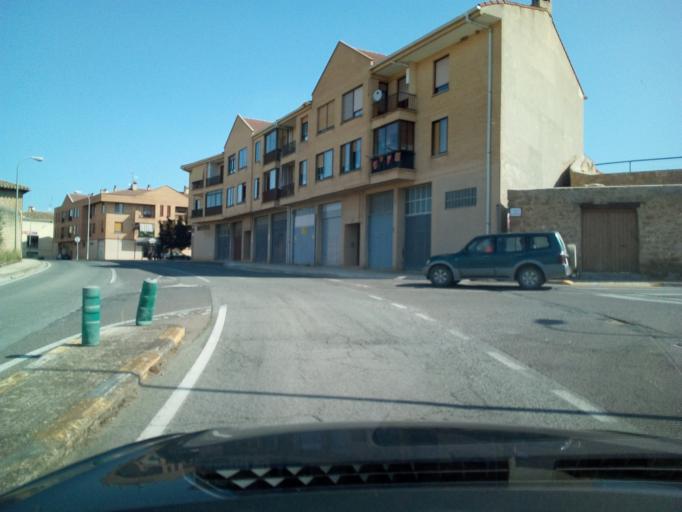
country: ES
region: Navarre
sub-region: Provincia de Navarra
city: Olite
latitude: 42.4775
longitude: -1.6490
